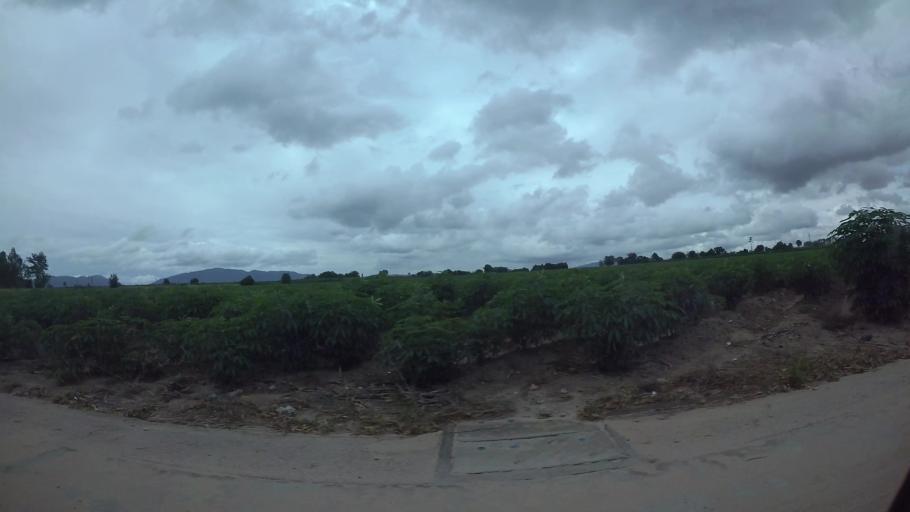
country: TH
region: Chon Buri
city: Si Racha
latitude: 13.1735
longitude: 100.9837
